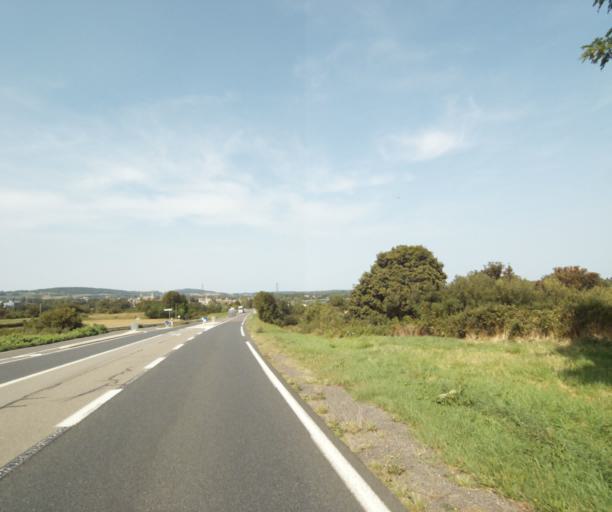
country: FR
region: Bourgogne
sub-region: Departement de Saone-et-Loire
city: Tournus
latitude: 46.5487
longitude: 4.9181
